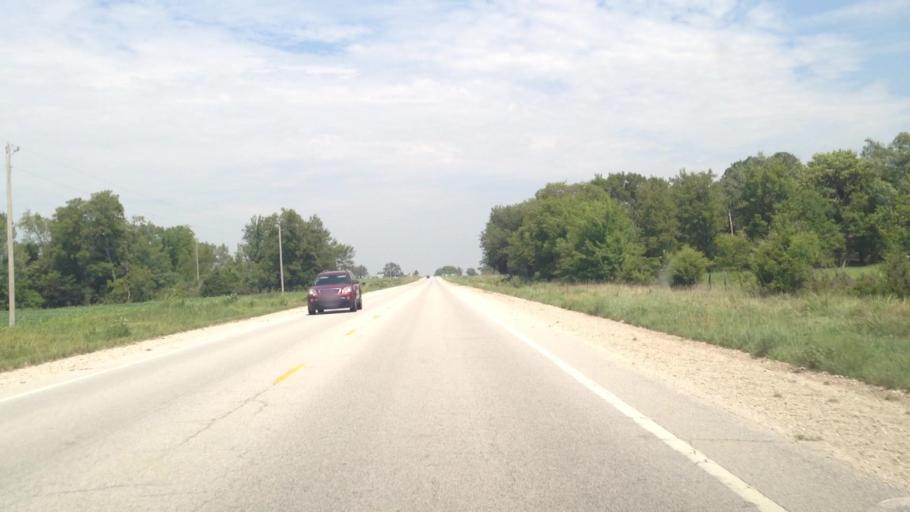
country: US
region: Kansas
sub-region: Neosho County
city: Erie
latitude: 37.4661
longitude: -95.2694
